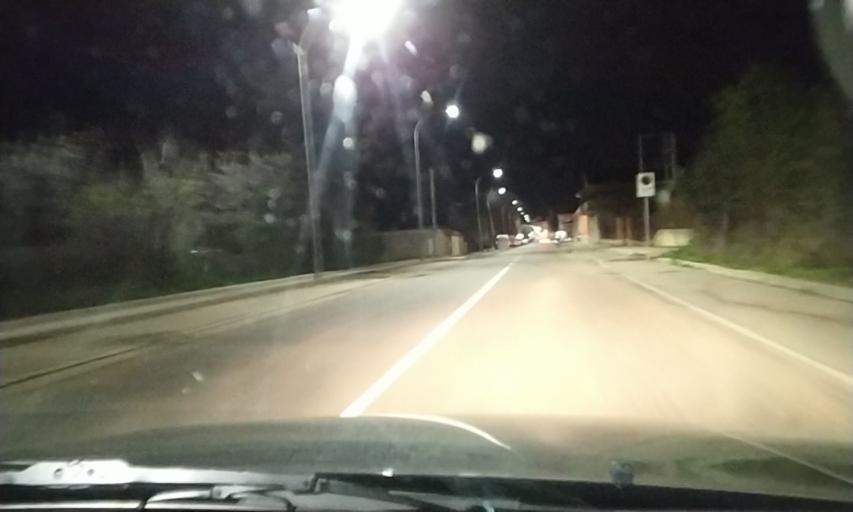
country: ES
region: Castille and Leon
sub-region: Provincia de Zamora
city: Benavente
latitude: 42.0086
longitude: -5.6700
